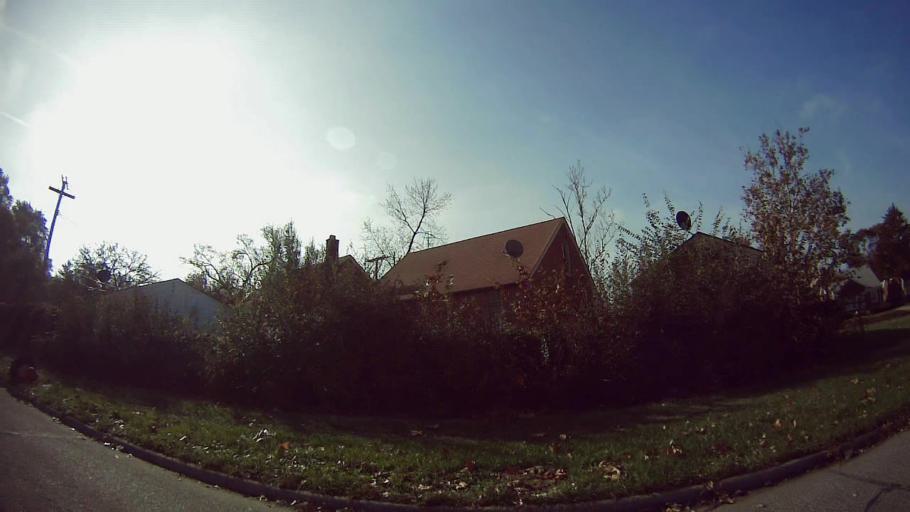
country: US
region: Michigan
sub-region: Oakland County
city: Oak Park
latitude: 42.4332
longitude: -83.1899
